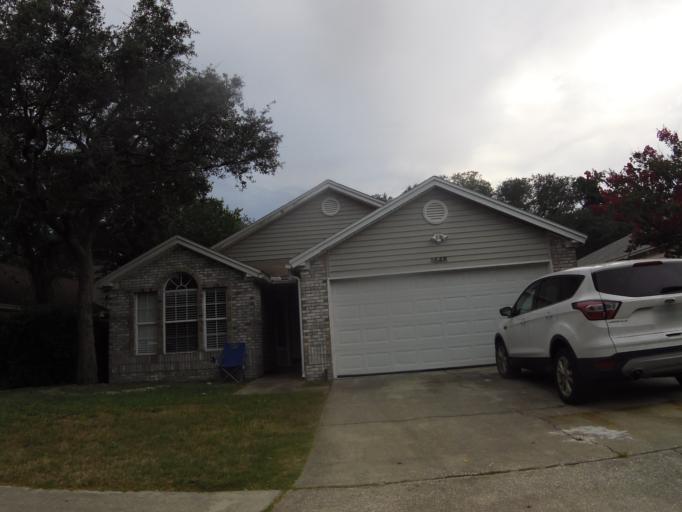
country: US
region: Florida
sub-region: Duval County
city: Jacksonville Beach
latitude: 30.2715
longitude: -81.4006
